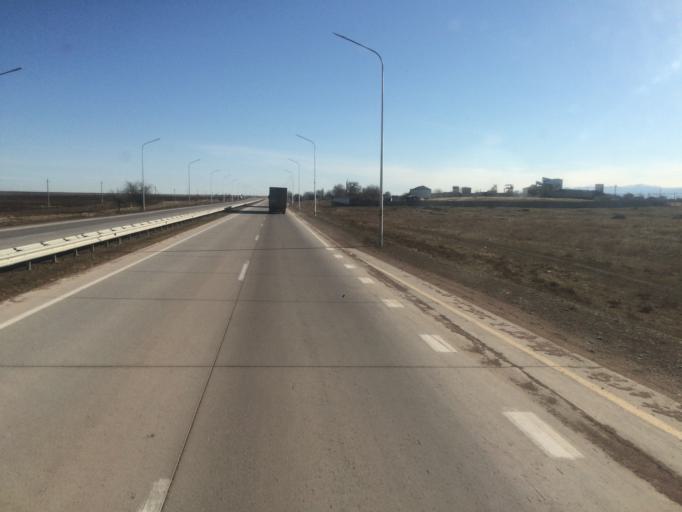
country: KZ
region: Zhambyl
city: Kulan
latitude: 42.9930
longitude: 72.3138
